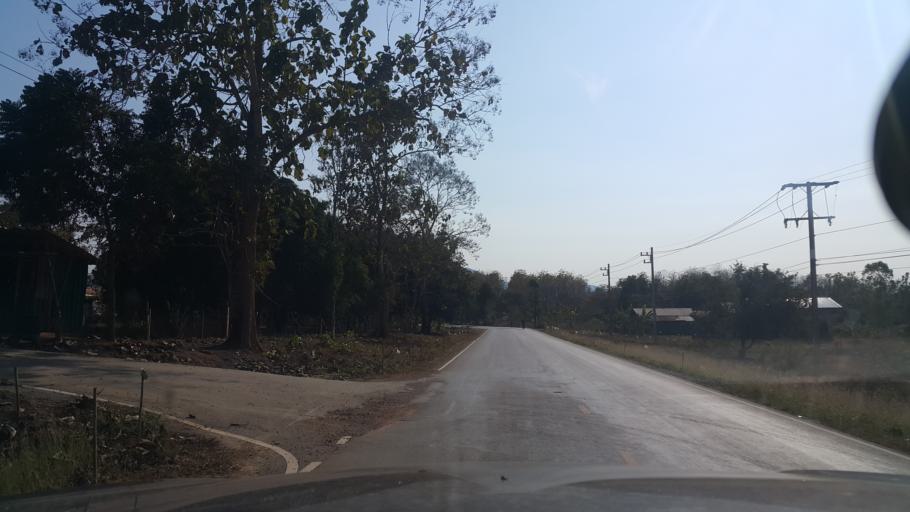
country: TH
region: Loei
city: Chiang Khan
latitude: 17.8507
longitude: 101.6530
